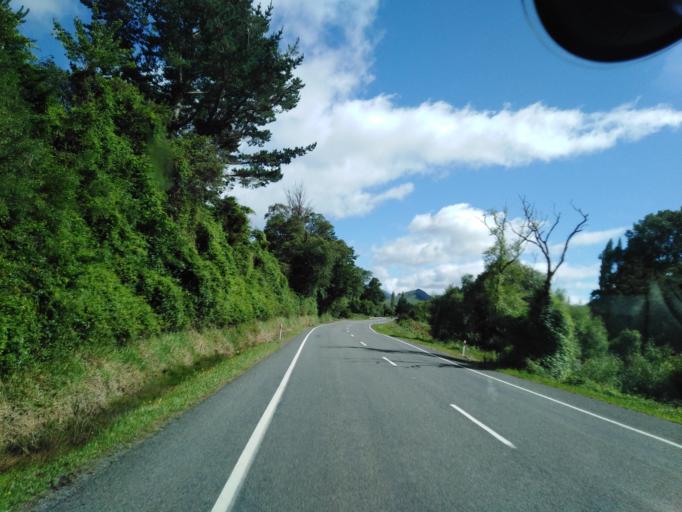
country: NZ
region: Nelson
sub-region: Nelson City
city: Nelson
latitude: -41.2517
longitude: 173.5775
